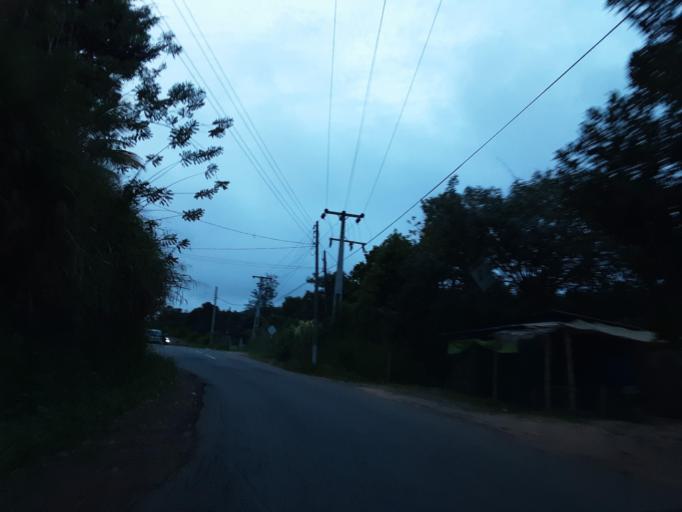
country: LK
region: Uva
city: Haputale
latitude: 6.9096
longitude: 80.9223
